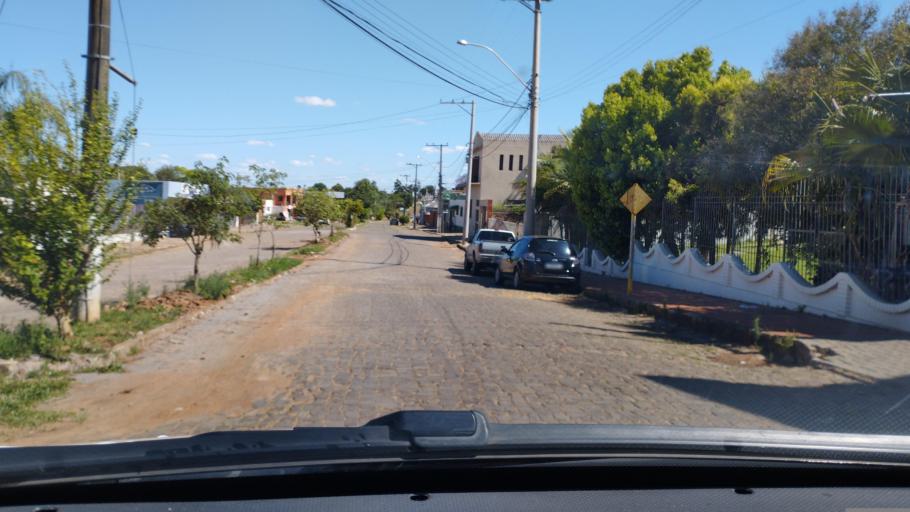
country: BR
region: Rio Grande do Sul
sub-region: Tupancireta
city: Tupancireta
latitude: -29.0877
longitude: -53.8349
